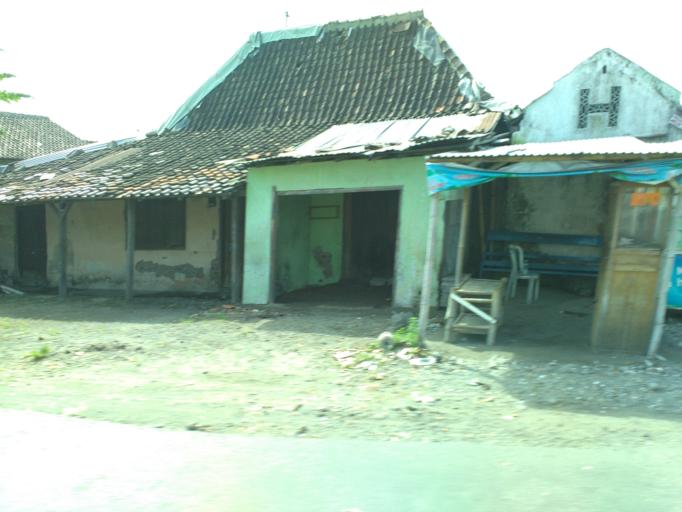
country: ID
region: Central Java
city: Jogonalan
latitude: -7.7409
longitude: 110.5327
